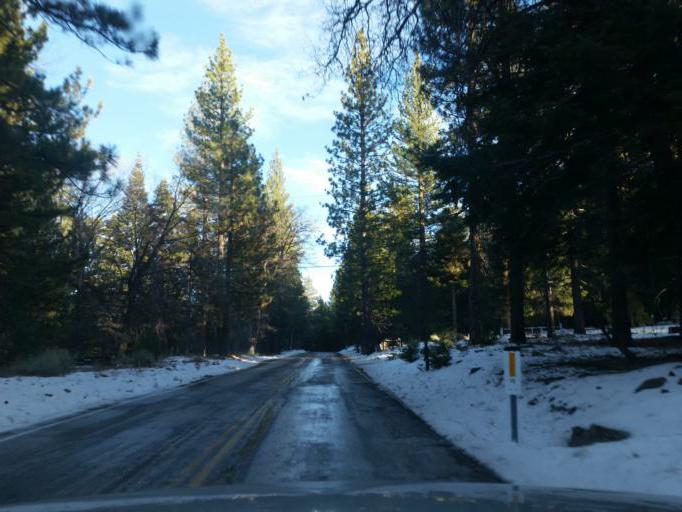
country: US
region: California
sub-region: San Bernardino County
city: Big Bear Lake
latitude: 34.1625
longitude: -116.8948
